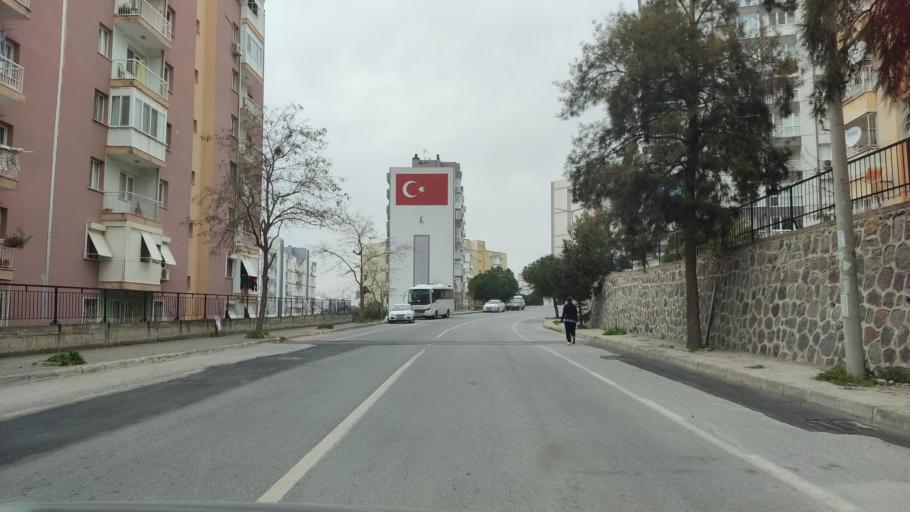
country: TR
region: Izmir
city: Karsiyaka
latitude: 38.5037
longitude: 27.0726
